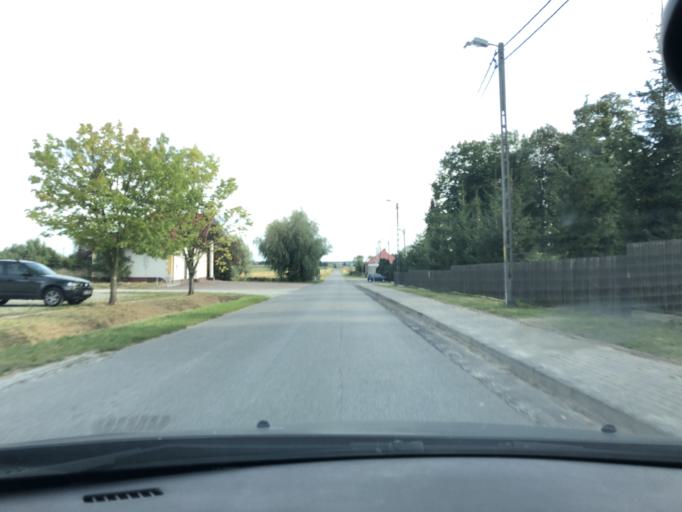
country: PL
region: Lodz Voivodeship
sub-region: Powiat wieruszowski
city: Walichnowy
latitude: 51.2611
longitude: 18.3940
